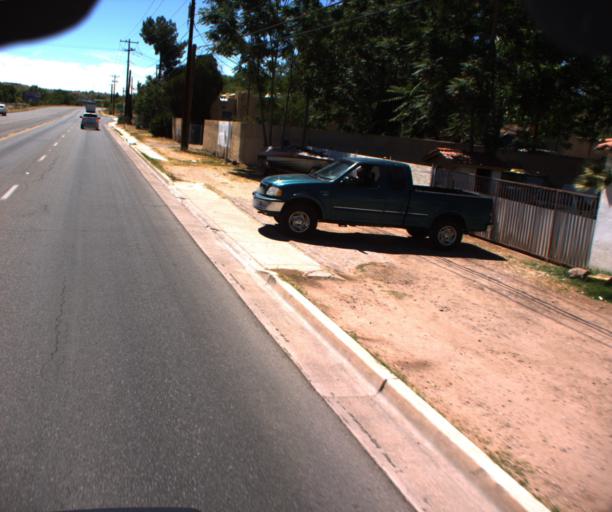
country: US
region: Arizona
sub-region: Santa Cruz County
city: Nogales
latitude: 31.3742
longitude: -110.9355
